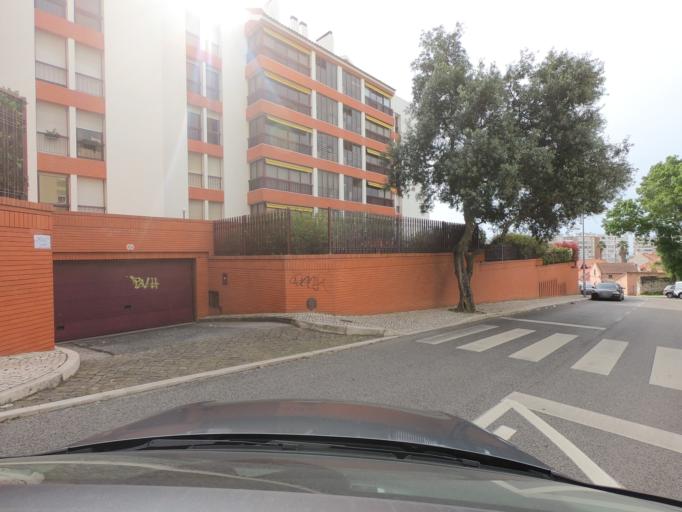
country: PT
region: Lisbon
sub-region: Oeiras
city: Oeiras
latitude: 38.6947
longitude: -9.3023
